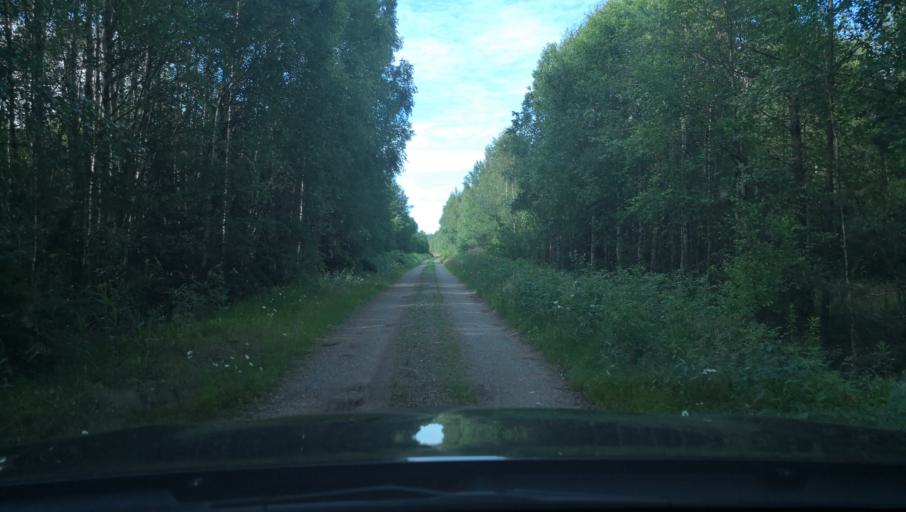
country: SE
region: Vaestmanland
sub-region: Surahammars Kommun
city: Surahammar
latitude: 59.6631
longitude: 16.1061
